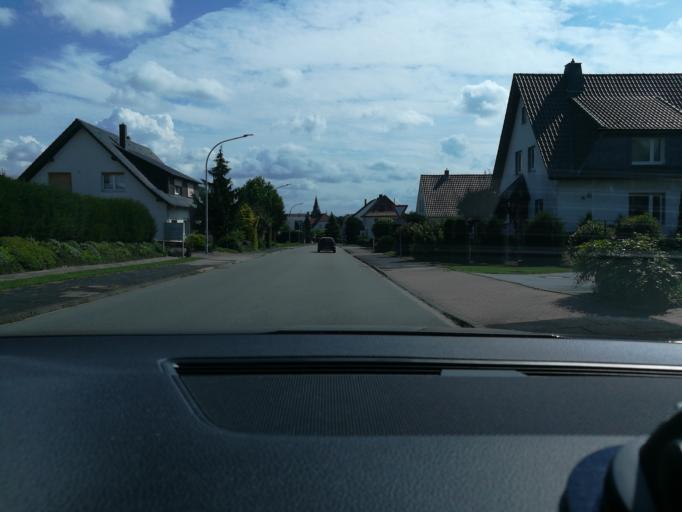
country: DE
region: North Rhine-Westphalia
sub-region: Regierungsbezirk Detmold
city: Huellhorst
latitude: 52.2762
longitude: 8.7046
